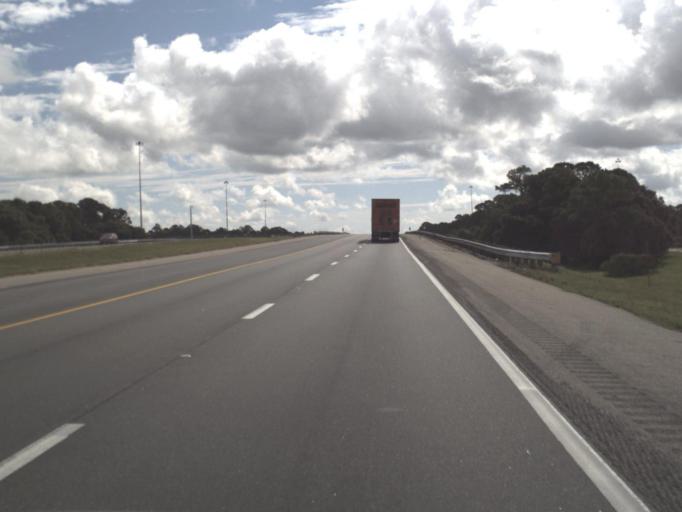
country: US
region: Florida
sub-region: Sarasota County
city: North Port
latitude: 27.0991
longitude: -82.2064
